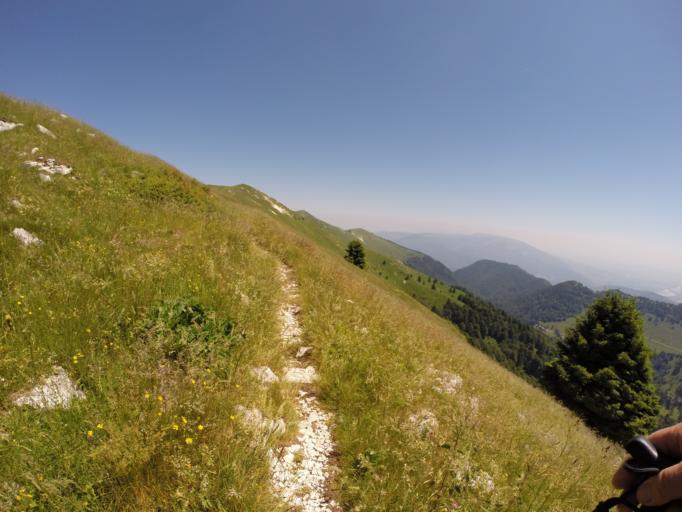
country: IT
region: Veneto
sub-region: Provincia di Treviso
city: Crespano del Grappa
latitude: 45.9042
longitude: 11.8227
